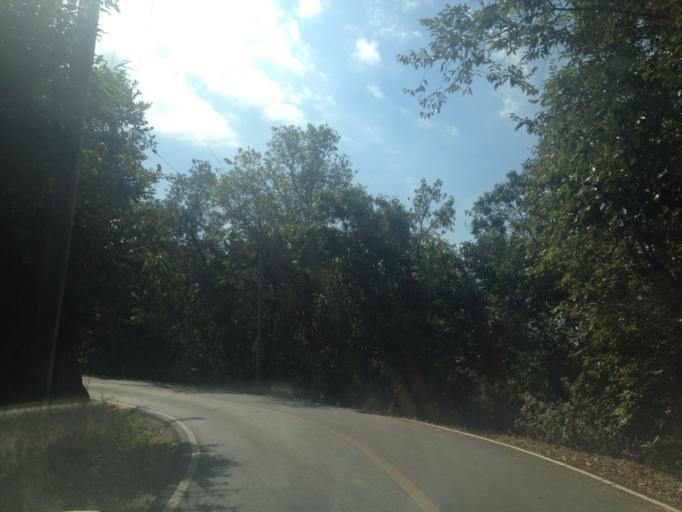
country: TH
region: Mae Hong Son
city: Ban Huai I Huak
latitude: 18.1326
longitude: 98.1448
